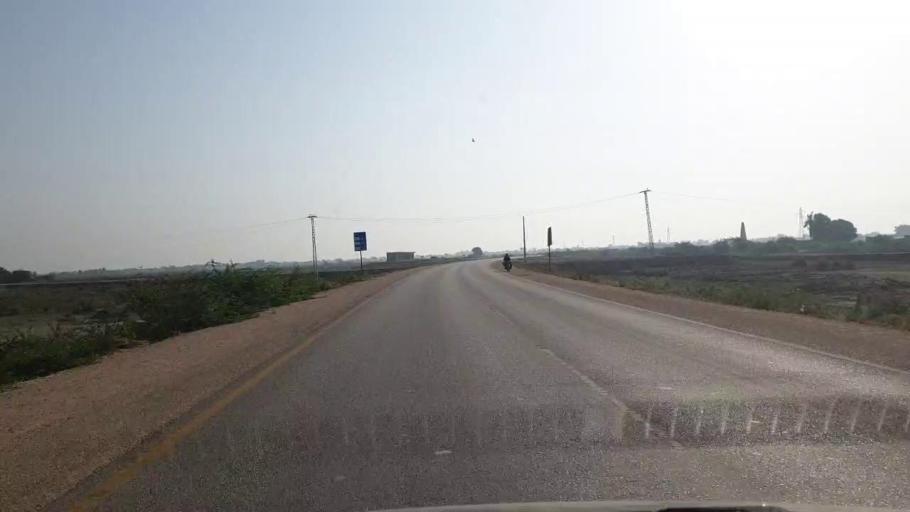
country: PK
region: Sindh
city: Badin
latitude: 24.6811
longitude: 68.8374
